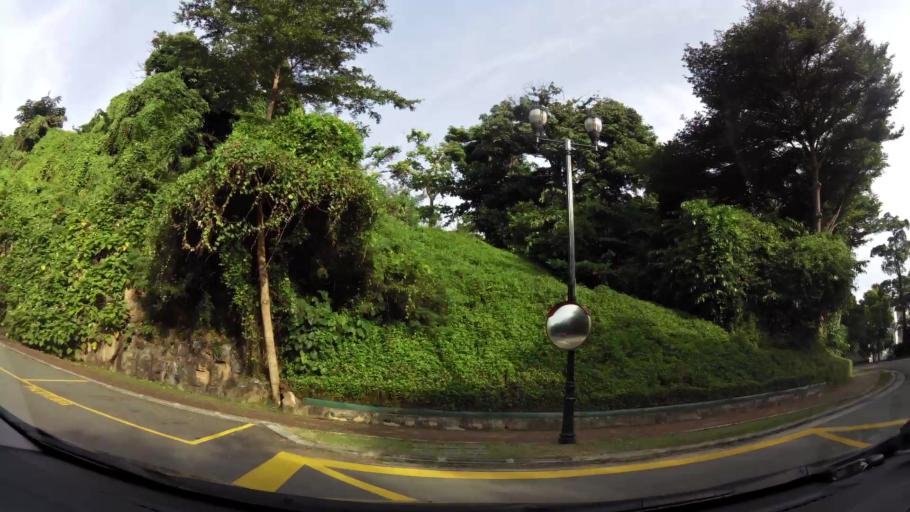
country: SG
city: Singapore
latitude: 1.2443
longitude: 103.8394
